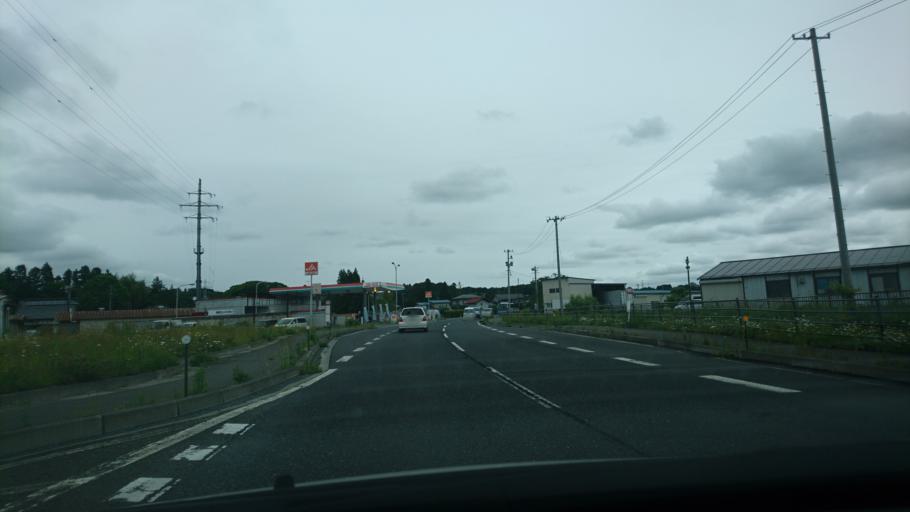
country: JP
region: Iwate
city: Ichinoseki
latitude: 39.0080
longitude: 141.1082
